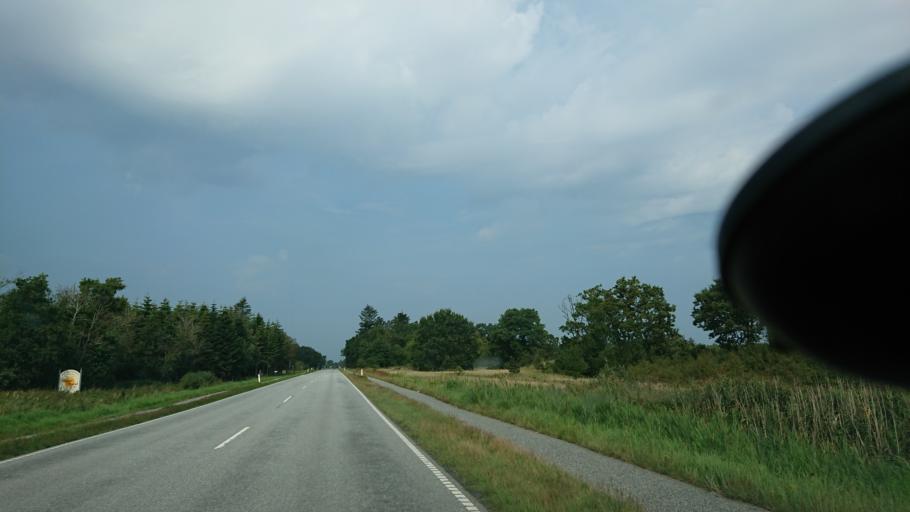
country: DK
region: North Denmark
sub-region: Frederikshavn Kommune
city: Strandby
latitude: 57.5172
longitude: 10.4310
